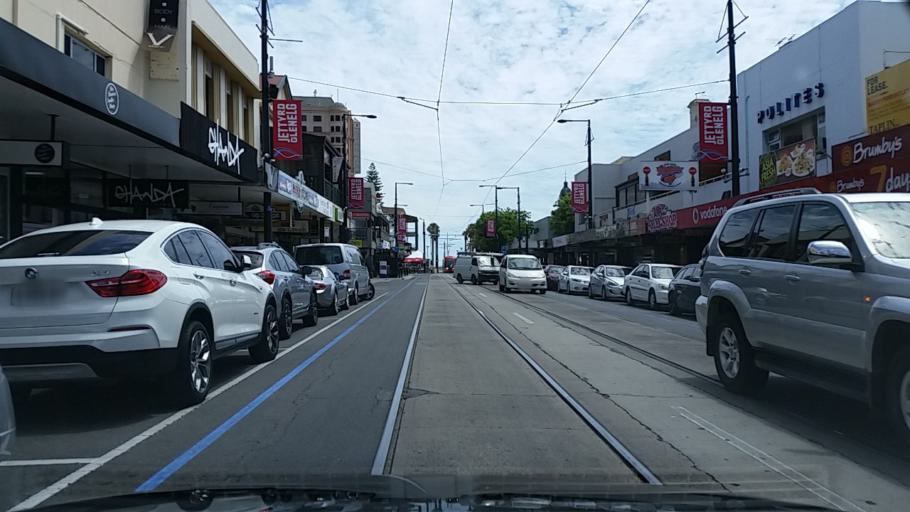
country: AU
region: South Australia
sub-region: Adelaide
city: Glenelg
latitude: -34.9803
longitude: 138.5137
